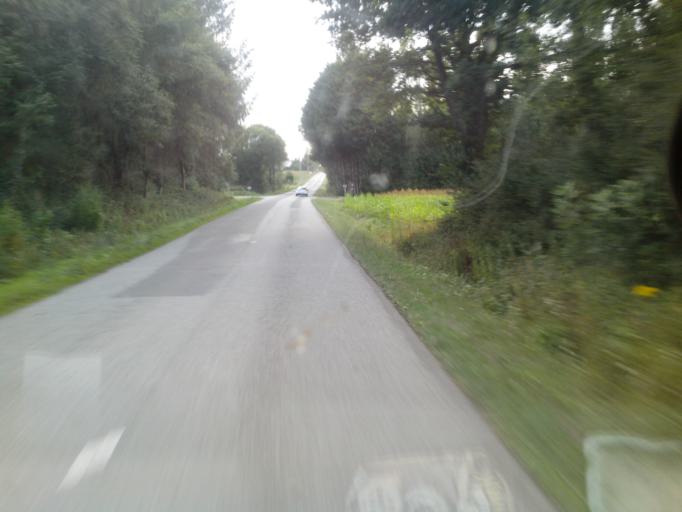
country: FR
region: Brittany
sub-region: Departement du Morbihan
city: Mauron
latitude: 48.0729
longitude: -2.2438
